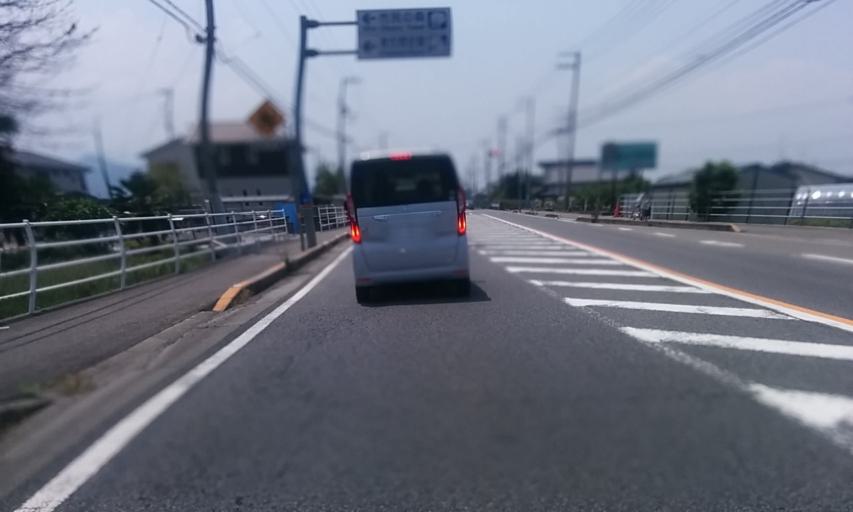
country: JP
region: Ehime
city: Saijo
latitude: 33.9114
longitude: 133.1996
